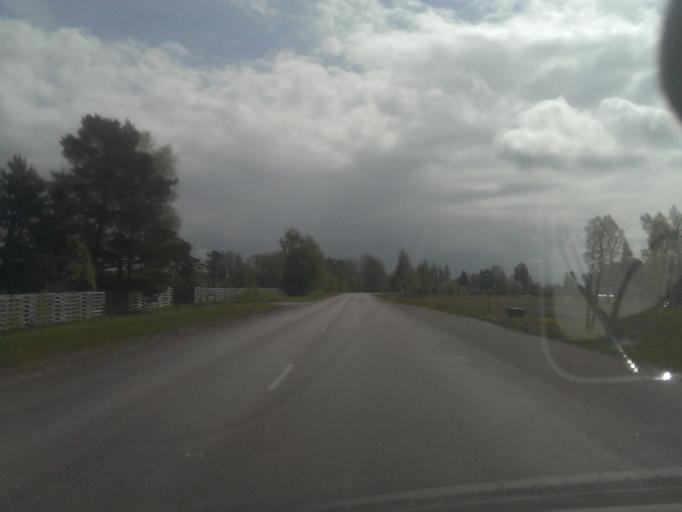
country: LV
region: Ventspils
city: Ventspils
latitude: 57.2844
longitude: 21.5705
